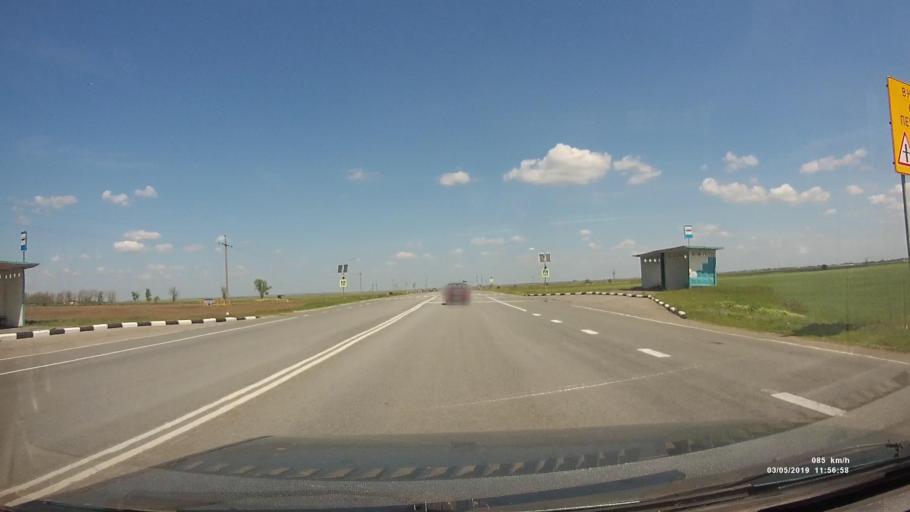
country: RU
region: Rostov
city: Bagayevskaya
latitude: 47.2016
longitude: 40.3063
